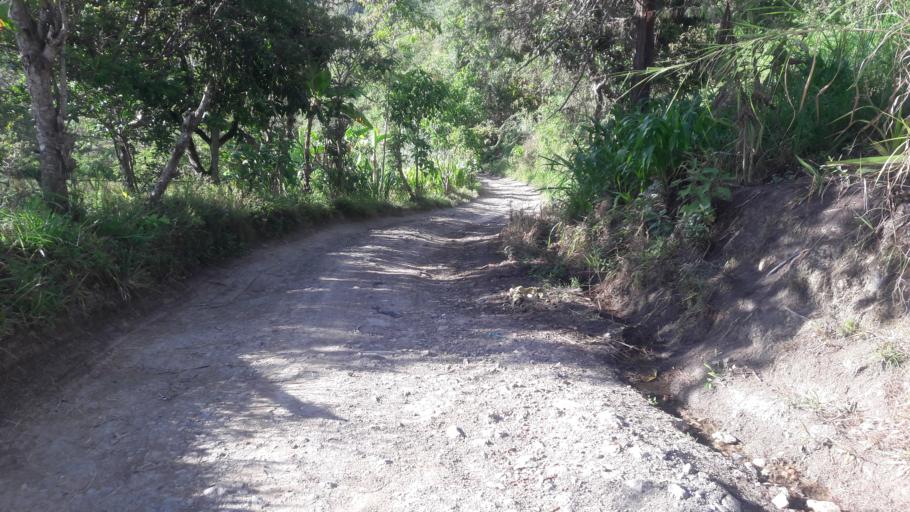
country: CO
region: Cundinamarca
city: Tenza
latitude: 5.0855
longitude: -73.4164
